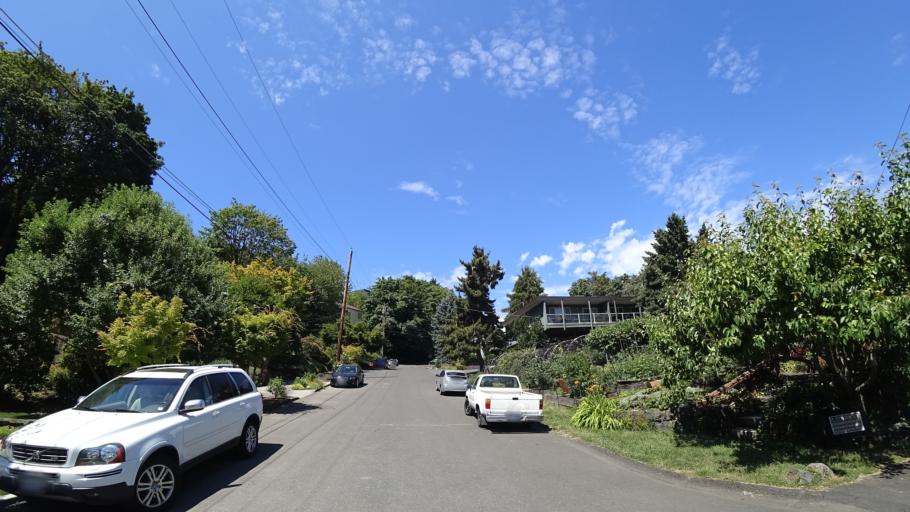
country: US
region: Oregon
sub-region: Multnomah County
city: Portland
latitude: 45.5325
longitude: -122.7068
